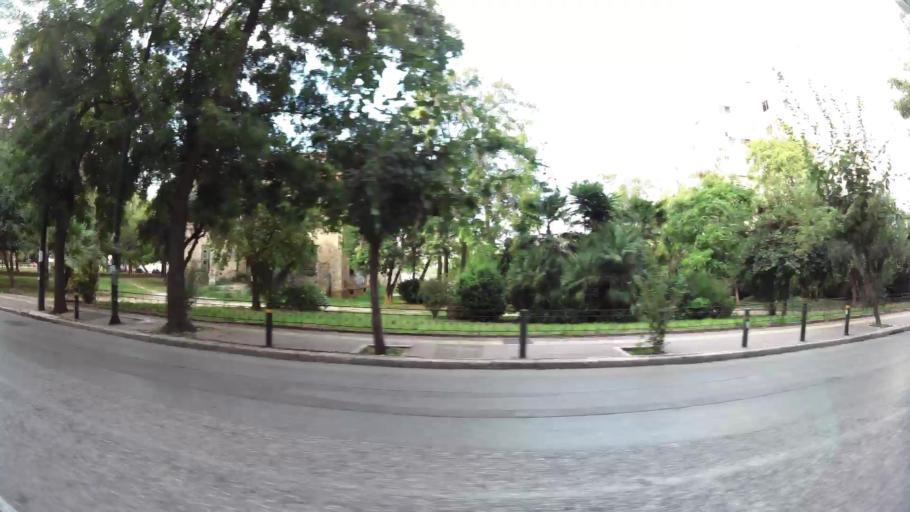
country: GR
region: Attica
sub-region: Nomarchia Athinas
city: Nea Chalkidona
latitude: 38.0175
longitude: 23.7354
